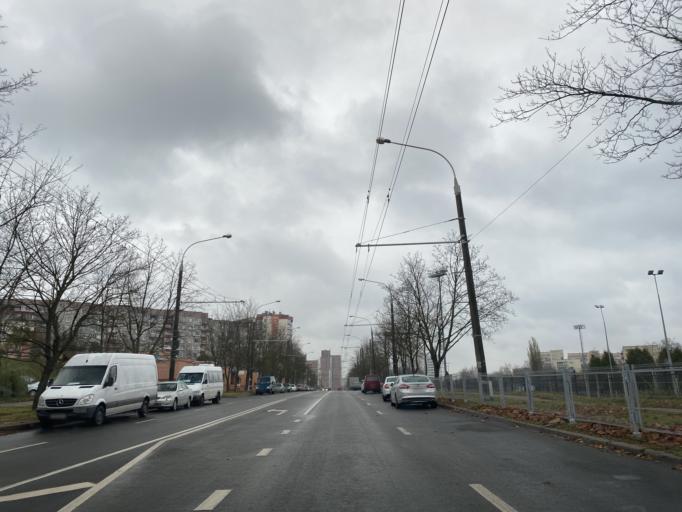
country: BY
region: Minsk
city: Bal'shavik
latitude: 53.9567
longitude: 27.6092
